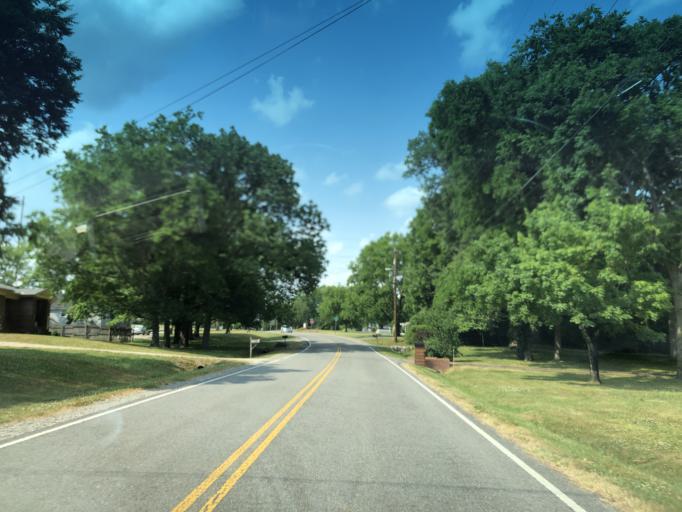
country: US
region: Tennessee
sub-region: Davidson County
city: Goodlettsville
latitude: 36.2470
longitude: -86.7252
